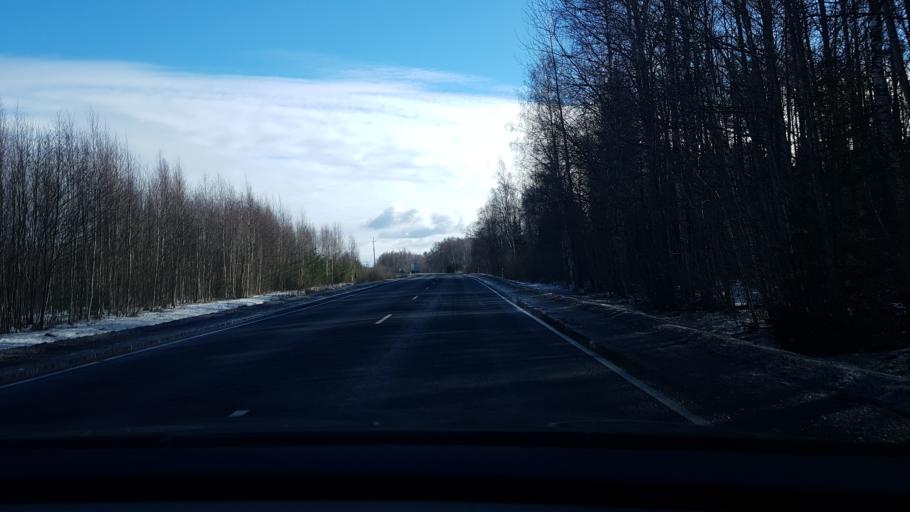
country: EE
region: Paernumaa
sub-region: Paikuse vald
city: Paikuse
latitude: 58.1951
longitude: 24.7501
